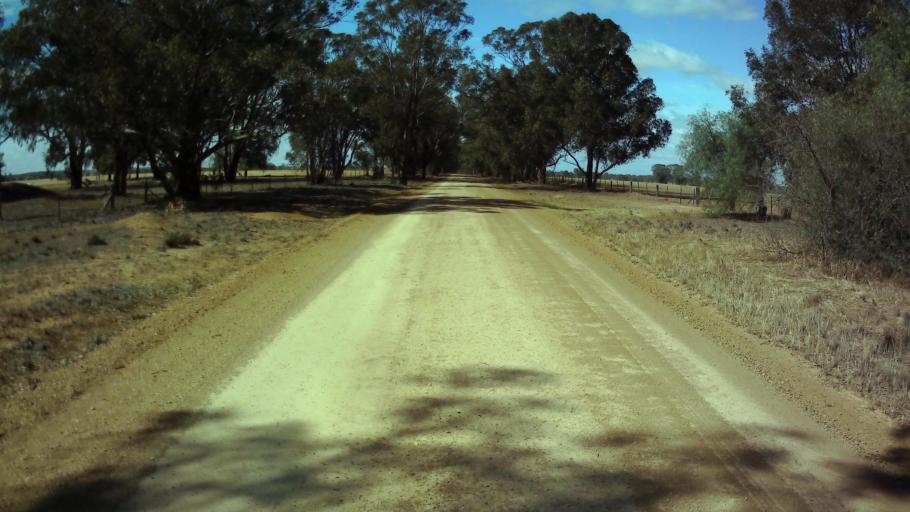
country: AU
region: New South Wales
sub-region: Weddin
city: Grenfell
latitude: -34.0457
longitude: 148.3148
